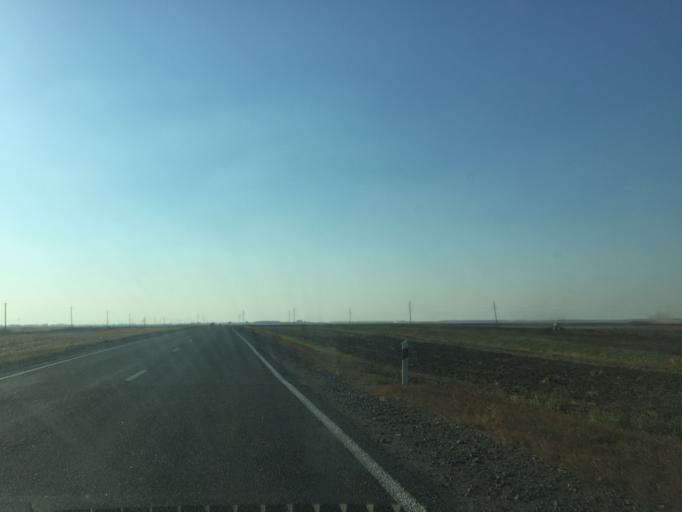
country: BY
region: Gomel
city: Dobrush
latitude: 52.3871
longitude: 31.4383
